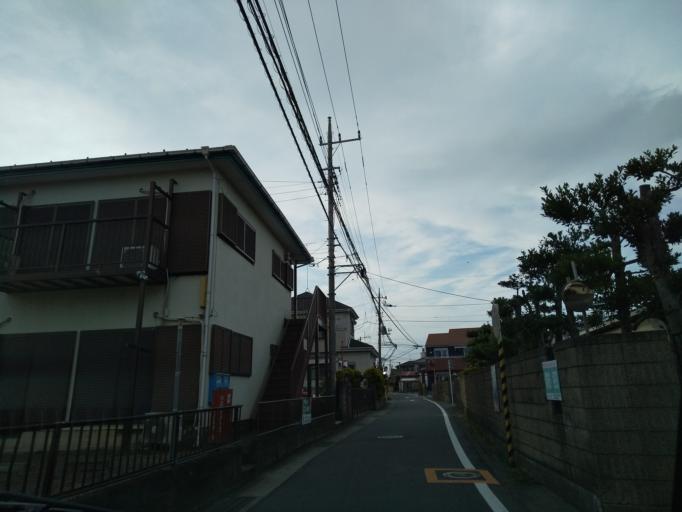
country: JP
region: Kanagawa
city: Zama
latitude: 35.5066
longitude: 139.3617
